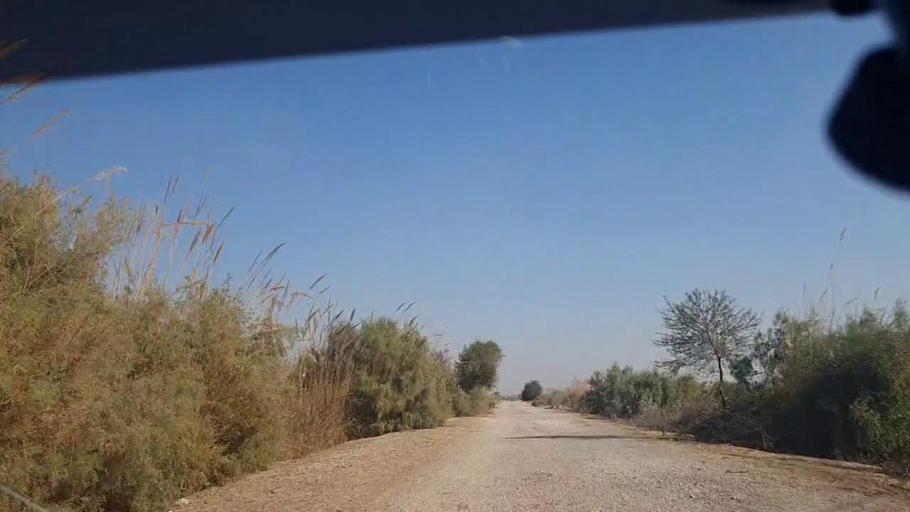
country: PK
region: Sindh
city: Khanpur
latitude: 27.5646
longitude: 69.3070
